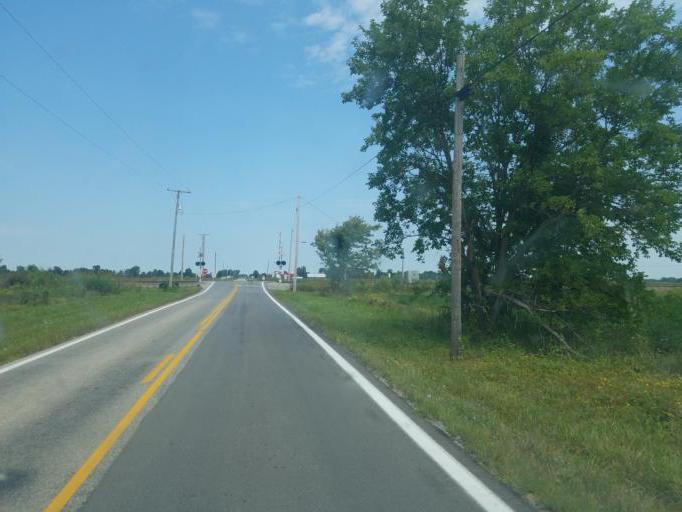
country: US
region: Ohio
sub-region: Marion County
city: Marion
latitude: 40.5852
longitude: -83.2174
